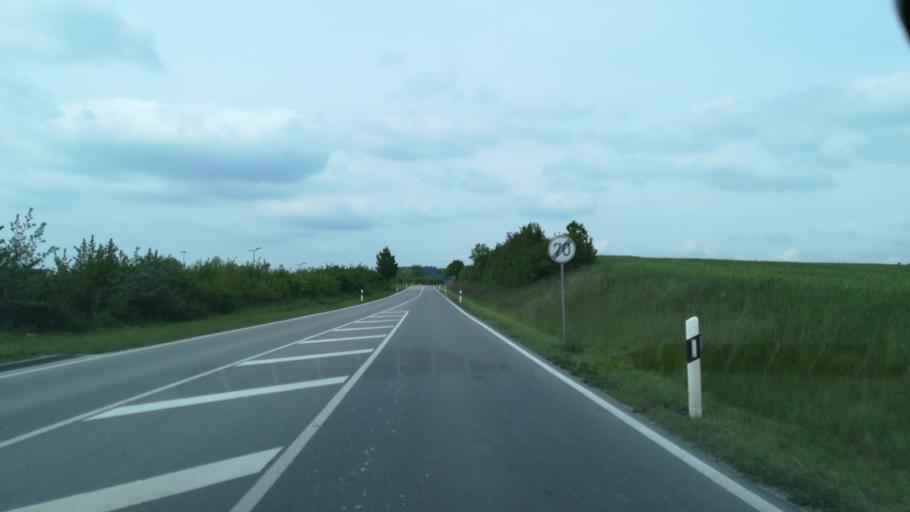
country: DE
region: Baden-Wuerttemberg
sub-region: Freiburg Region
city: Steisslingen
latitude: 47.7838
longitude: 8.9280
